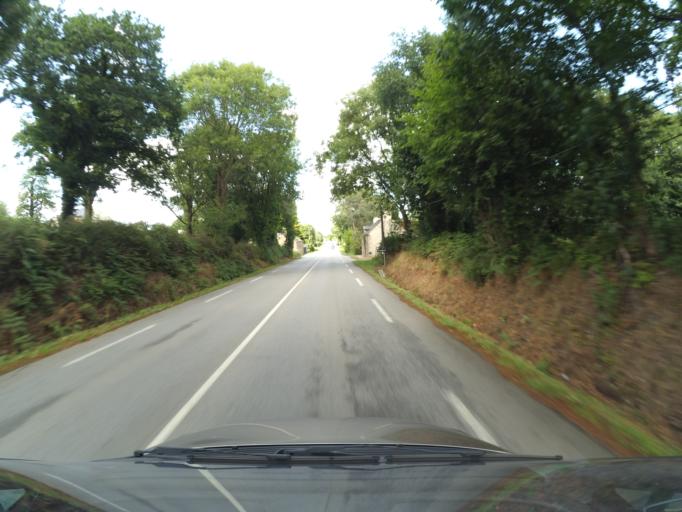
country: FR
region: Brittany
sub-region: Departement du Morbihan
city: Brech
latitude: 47.7227
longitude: -3.0113
